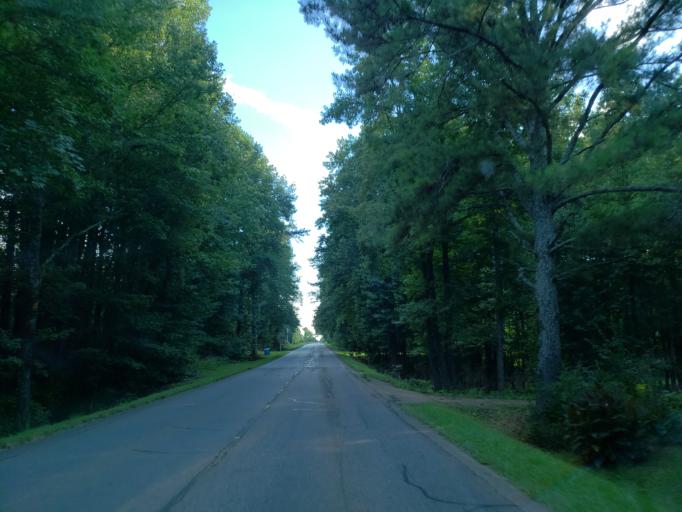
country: US
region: Georgia
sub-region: Cherokee County
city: Canton
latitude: 34.3505
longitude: -84.5060
